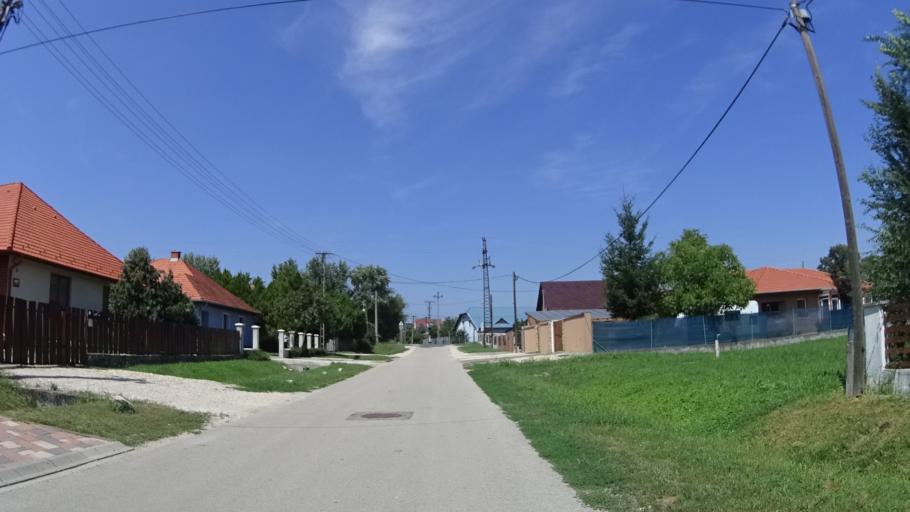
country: HU
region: Fejer
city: Pakozd
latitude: 47.2209
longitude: 18.5573
